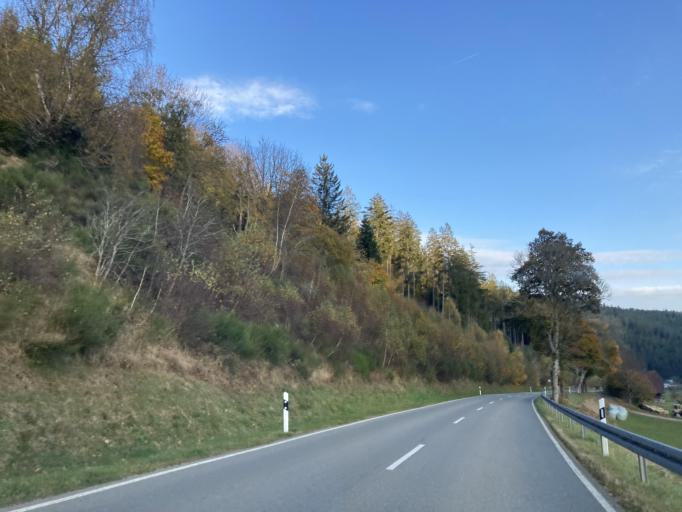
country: DE
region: Baden-Wuerttemberg
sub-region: Freiburg Region
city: Vohrenbach
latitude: 48.0074
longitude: 8.2907
